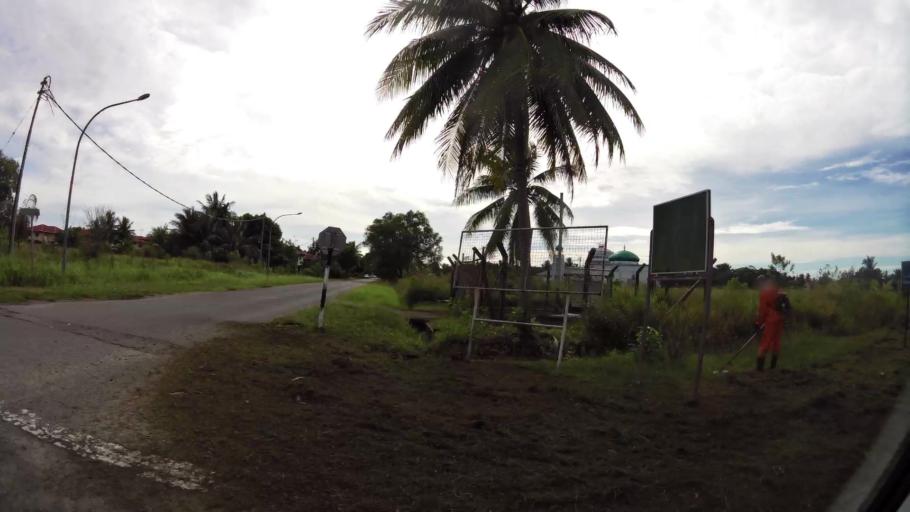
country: BN
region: Belait
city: Seria
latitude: 4.6006
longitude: 114.3267
